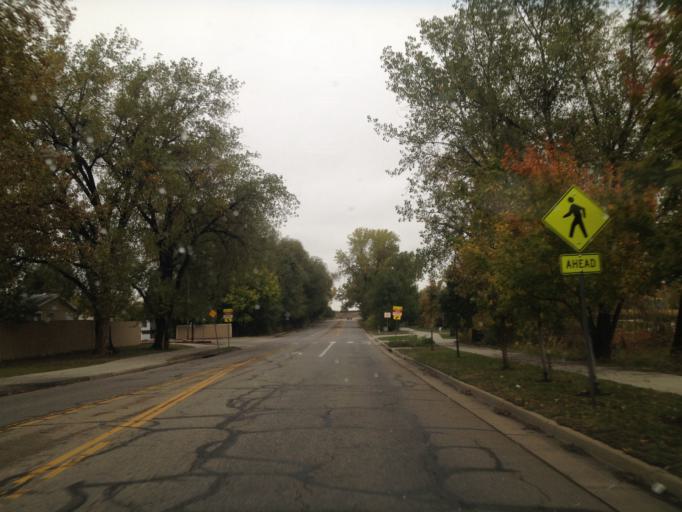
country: US
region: Colorado
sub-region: Boulder County
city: Boulder
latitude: 40.0302
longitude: -105.2346
